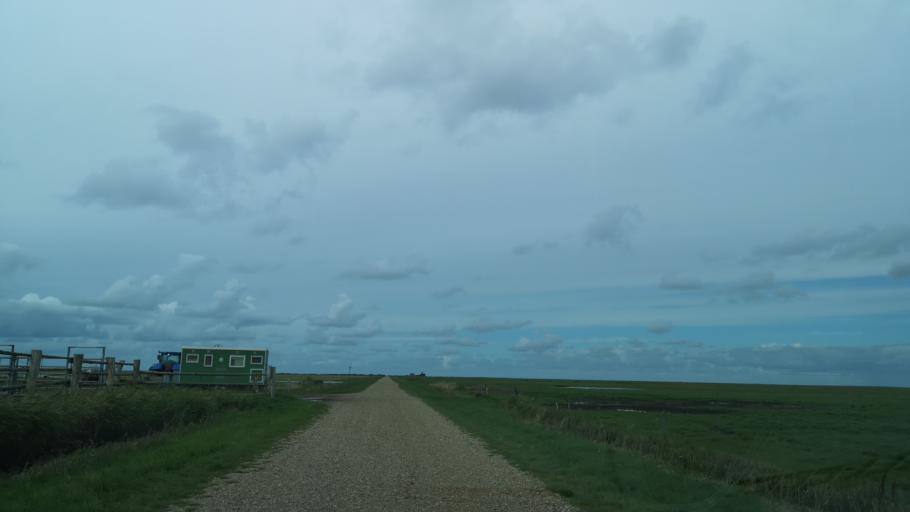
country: DK
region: Central Jutland
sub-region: Ringkobing-Skjern Kommune
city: Hvide Sande
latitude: 55.8772
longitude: 8.2251
